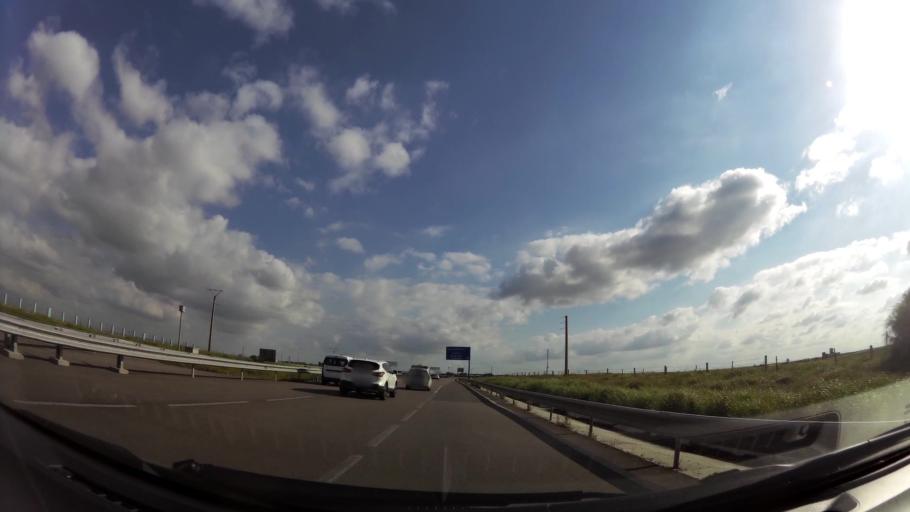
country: MA
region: Chaouia-Ouardigha
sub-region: Settat Province
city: Berrechid
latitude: 33.2282
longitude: -7.5735
